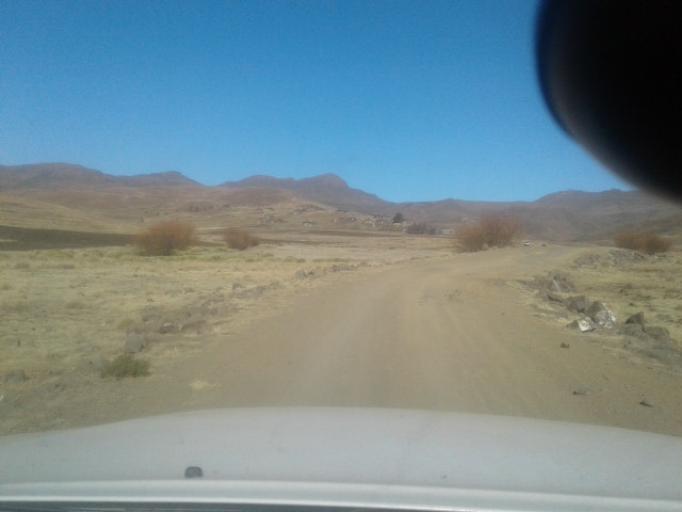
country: LS
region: Maseru
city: Nako
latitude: -29.3776
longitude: 28.0174
